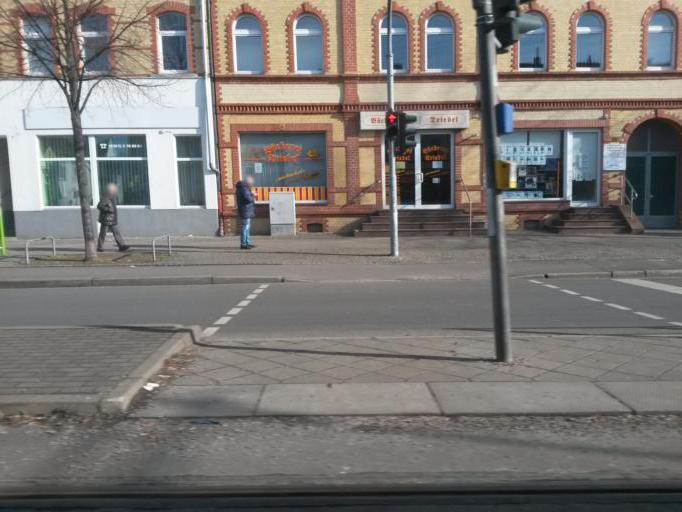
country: DE
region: Thuringia
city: Erfurt
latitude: 50.9948
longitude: 11.0259
